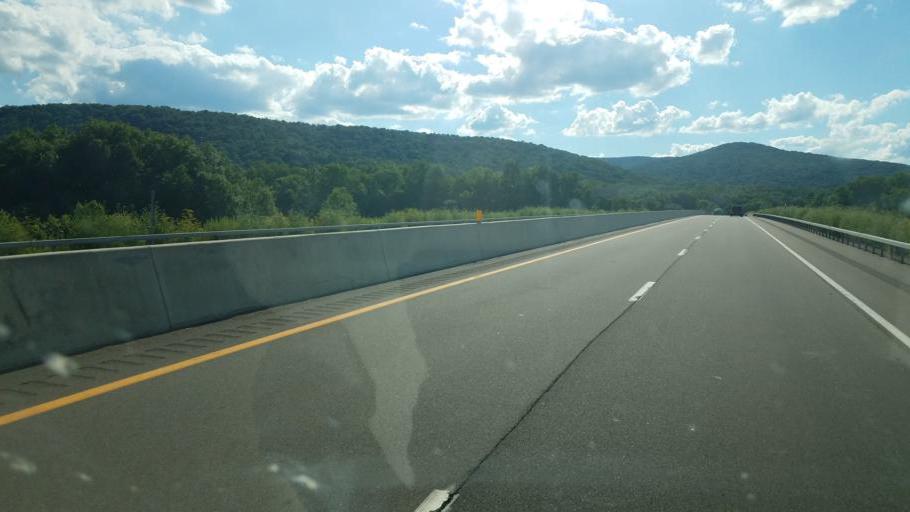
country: US
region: New York
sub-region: Cattaraugus County
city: Salamanca
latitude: 42.0906
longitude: -78.6427
